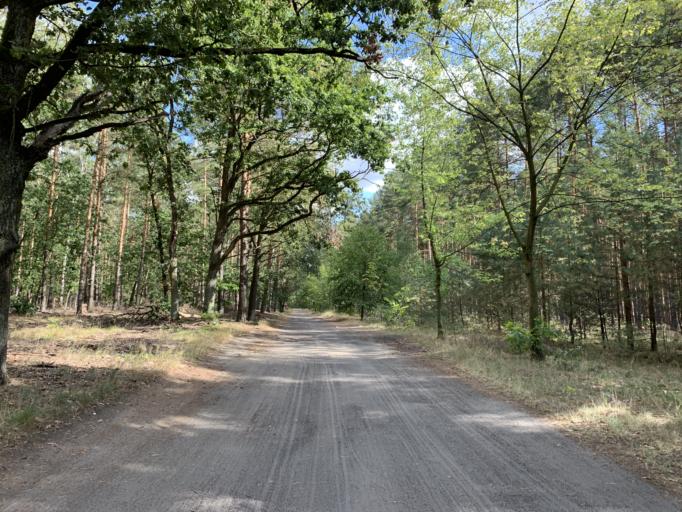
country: DE
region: Brandenburg
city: Michendorf
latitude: 52.3110
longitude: 12.9969
